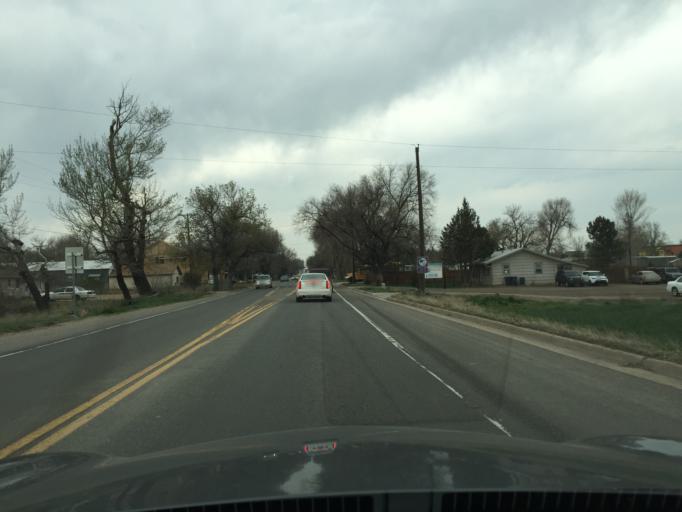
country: US
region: Colorado
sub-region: Boulder County
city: Lafayette
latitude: 40.0003
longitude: -105.0786
